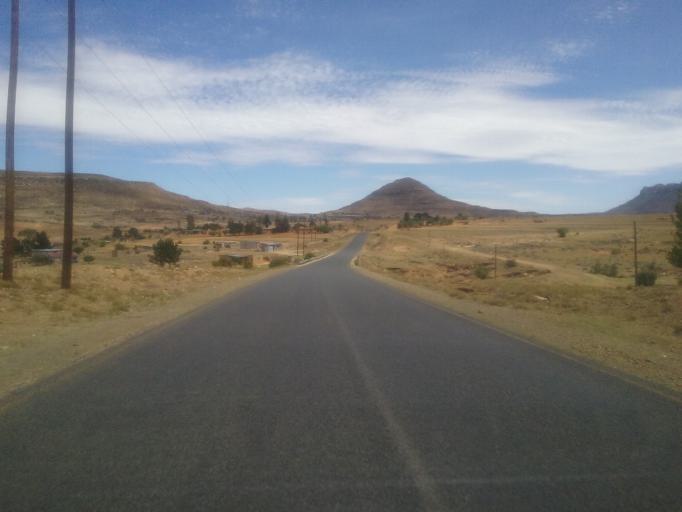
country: LS
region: Mafeteng
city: Mafeteng
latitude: -29.9693
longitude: 27.3071
